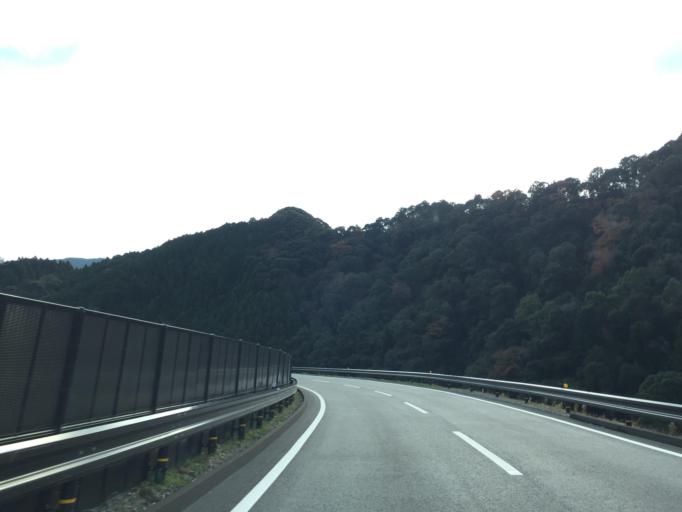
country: JP
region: Wakayama
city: Iwade
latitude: 34.1435
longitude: 135.3800
